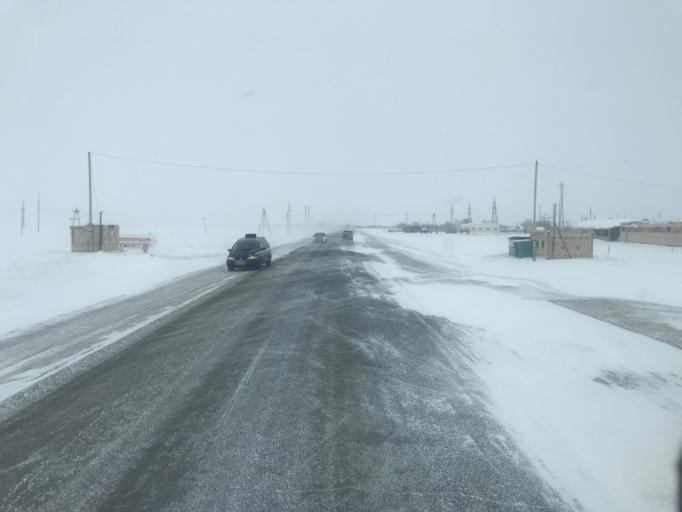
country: KZ
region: Batys Qazaqstan
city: Chapaev
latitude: 50.5142
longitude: 51.0583
